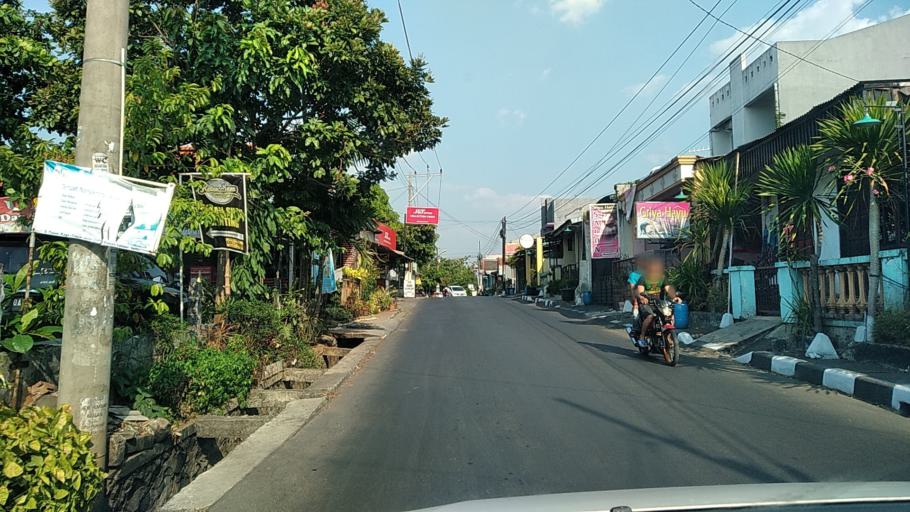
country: ID
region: Central Java
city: Ungaran
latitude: -7.0693
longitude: 110.4255
